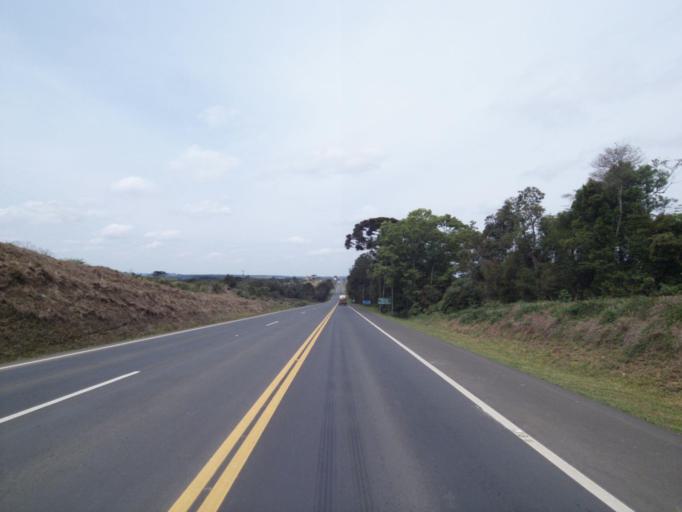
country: BR
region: Parana
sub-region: Irati
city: Irati
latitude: -25.4651
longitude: -50.5807
